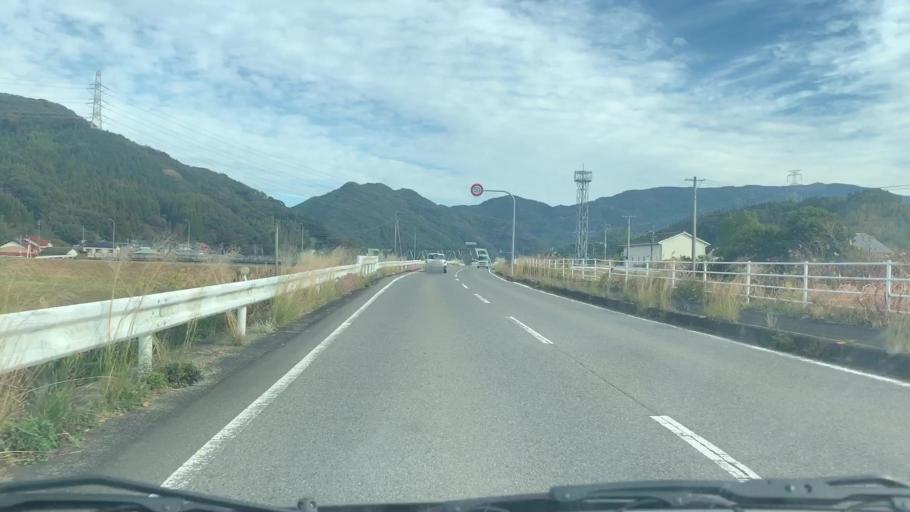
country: JP
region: Saga Prefecture
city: Karatsu
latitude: 33.3523
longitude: 130.0011
